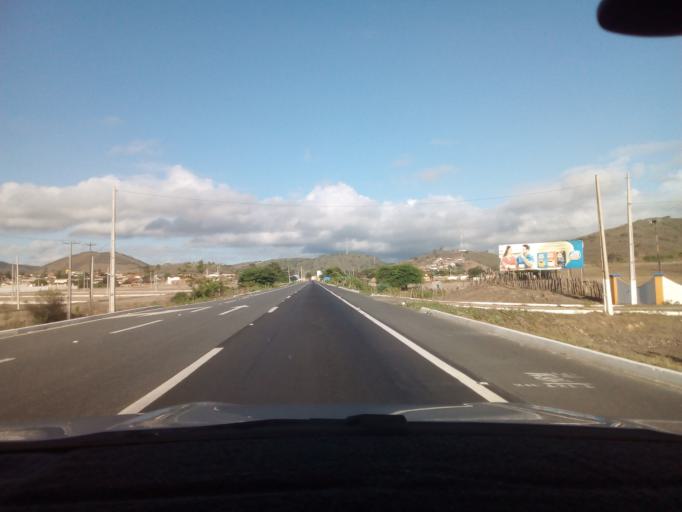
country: BR
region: Paraiba
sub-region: Inga
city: Inga
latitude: -7.2465
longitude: -35.6569
